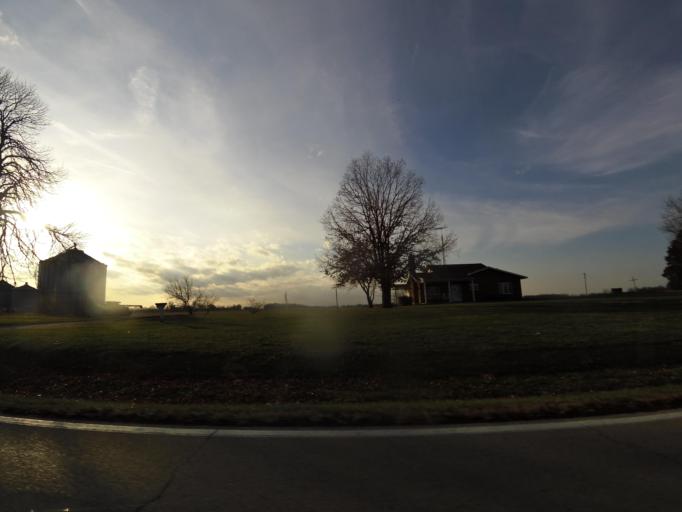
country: US
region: Illinois
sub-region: Fayette County
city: Vandalia
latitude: 38.9207
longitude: -89.2204
